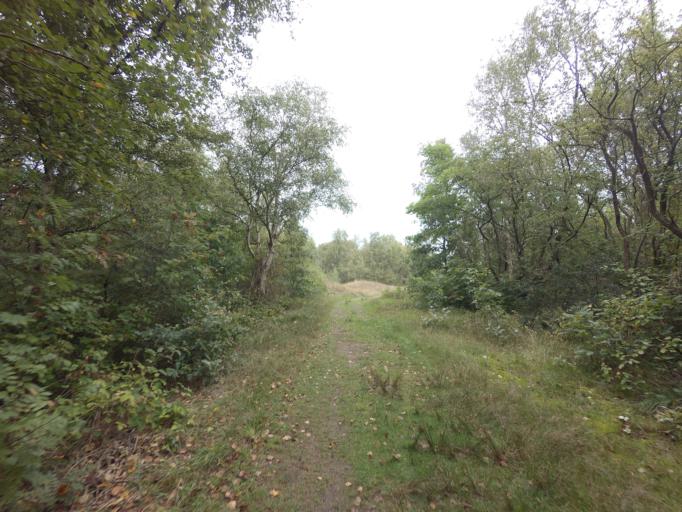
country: NL
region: Friesland
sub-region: Gemeente Schiermonnikoog
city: Schiermonnikoog
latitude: 53.4857
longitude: 6.1669
